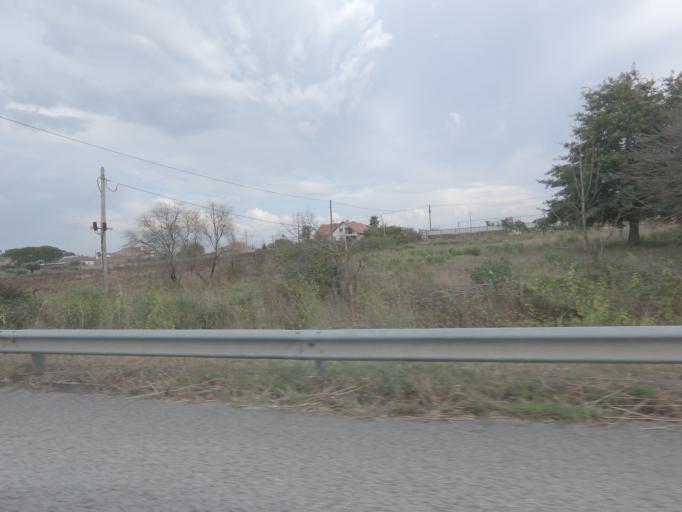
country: PT
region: Viseu
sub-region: Santa Comba Dao
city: Santa Comba Dao
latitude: 40.3737
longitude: -8.1264
